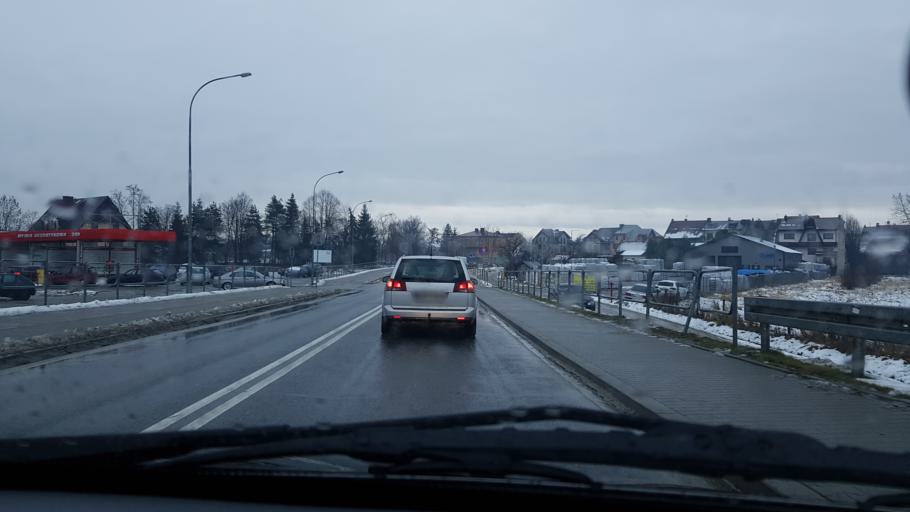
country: PL
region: Lesser Poland Voivodeship
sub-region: Powiat nowotarski
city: Nowy Targ
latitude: 49.4838
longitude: 20.0388
